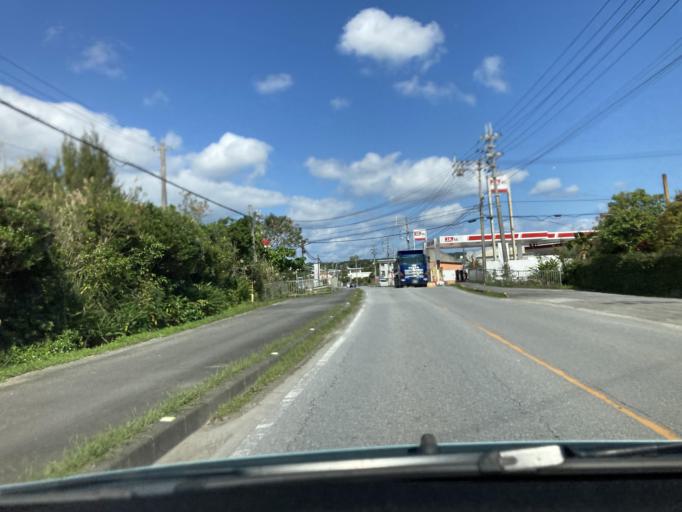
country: JP
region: Okinawa
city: Nago
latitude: 26.6152
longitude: 128.0004
